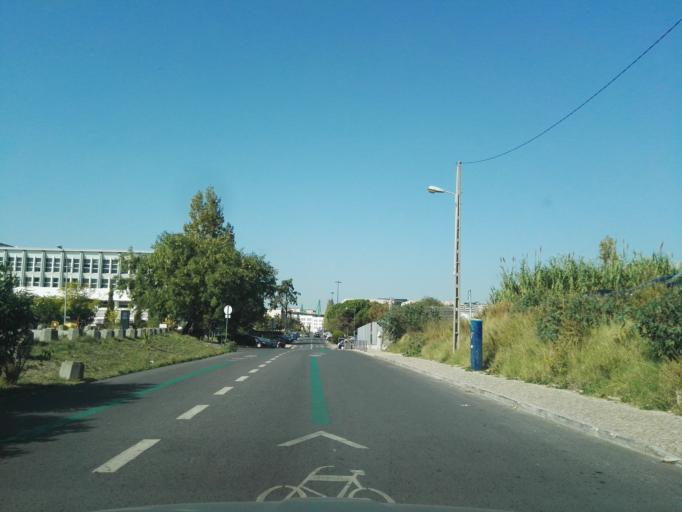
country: PT
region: Lisbon
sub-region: Lisbon
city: Lisbon
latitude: 38.7508
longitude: -9.1552
